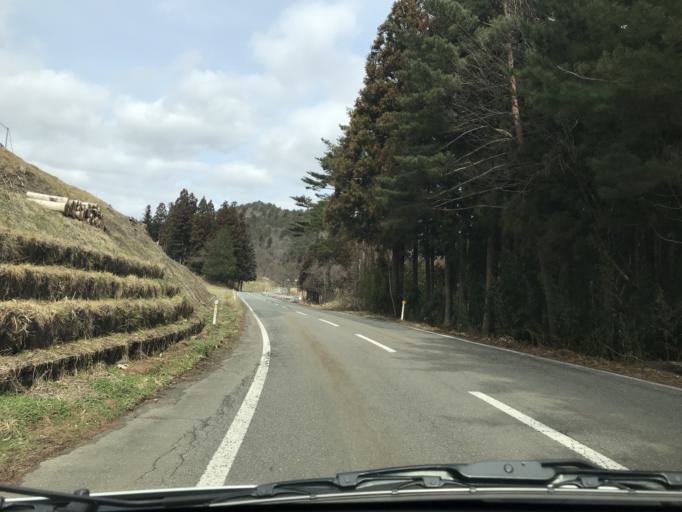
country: JP
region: Iwate
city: Kitakami
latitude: 39.2792
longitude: 141.3200
